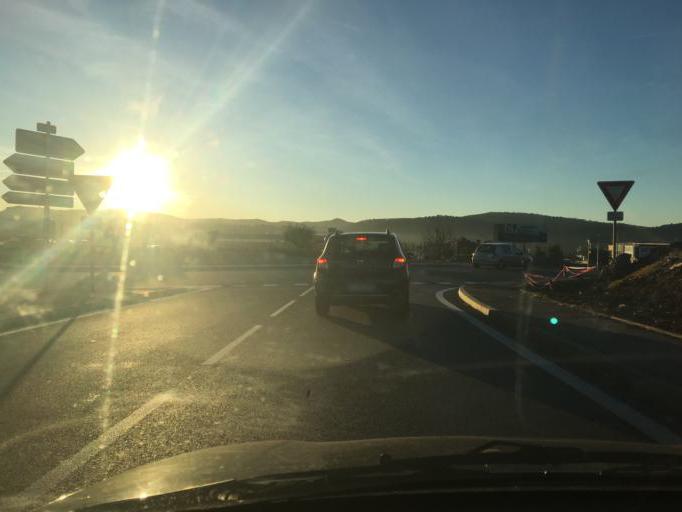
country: FR
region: Provence-Alpes-Cote d'Azur
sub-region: Departement du Var
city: Les Arcs
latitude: 43.4541
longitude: 6.4903
